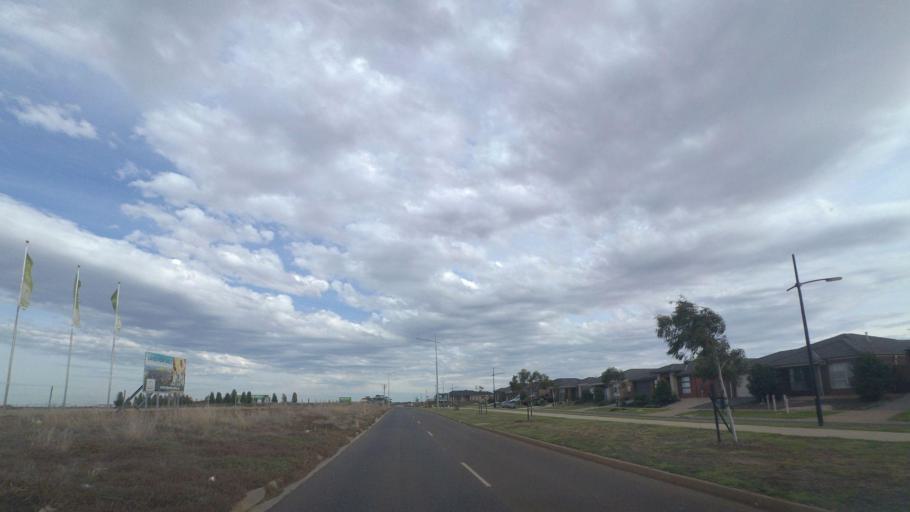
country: AU
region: Victoria
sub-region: Melton
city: Melton South
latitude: -37.7172
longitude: 144.5620
